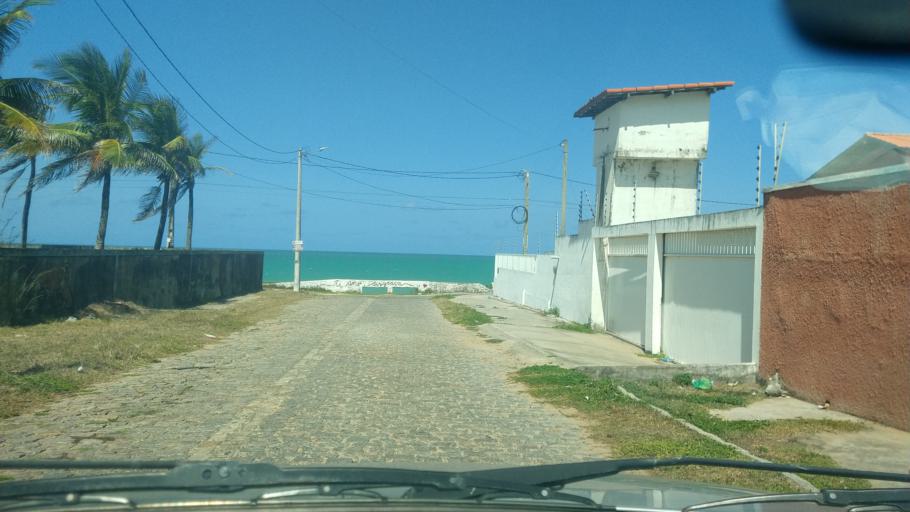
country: BR
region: Rio Grande do Norte
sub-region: Parnamirim
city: Parnamirim
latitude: -5.9514
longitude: -35.1531
